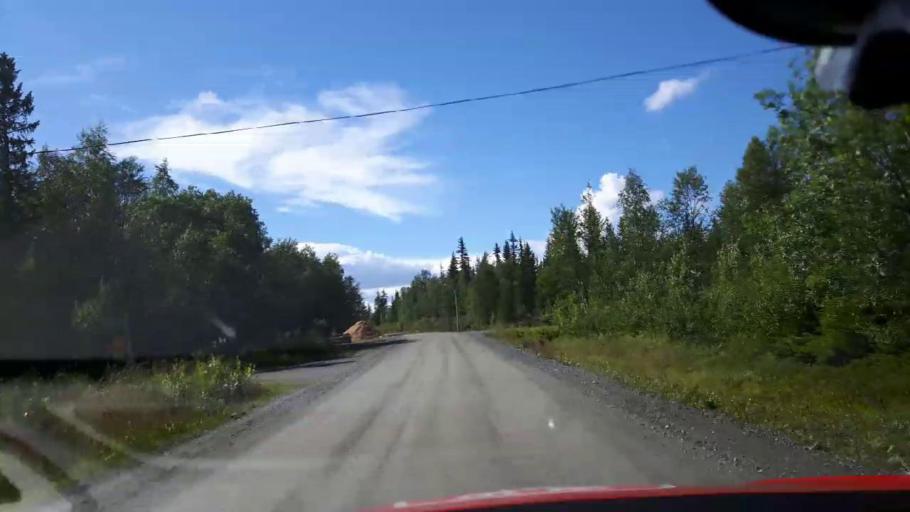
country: SE
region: Jaemtland
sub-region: Are Kommun
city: Are
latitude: 63.2183
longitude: 13.0695
